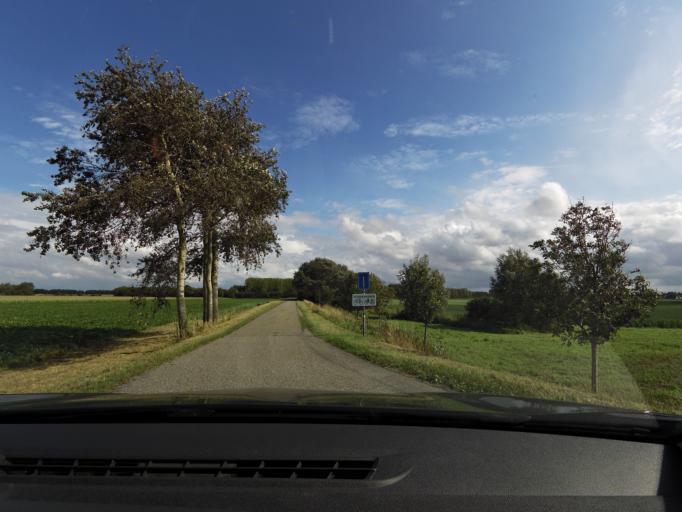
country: NL
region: South Holland
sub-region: Gemeente Goeree-Overflakkee
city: Goedereede
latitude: 51.8275
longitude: 3.9897
